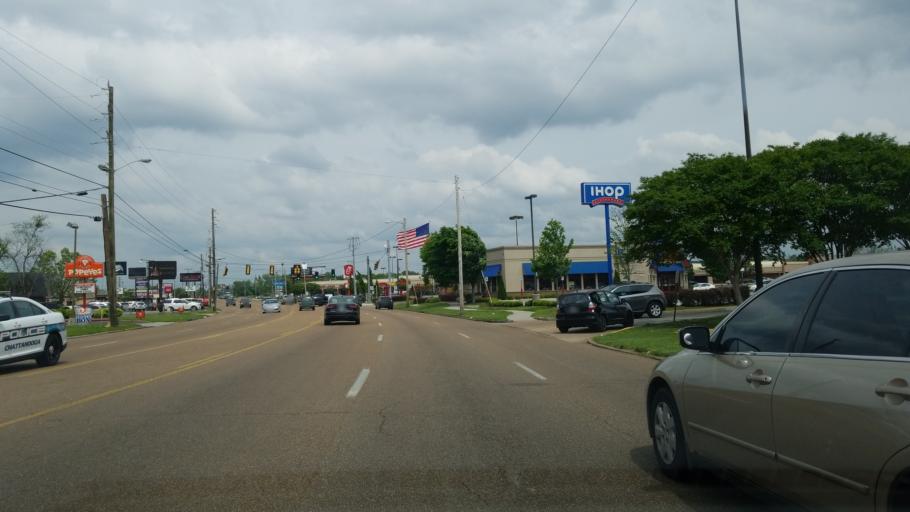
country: US
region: Tennessee
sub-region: Hamilton County
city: East Ridge
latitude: 35.0118
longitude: -85.2137
